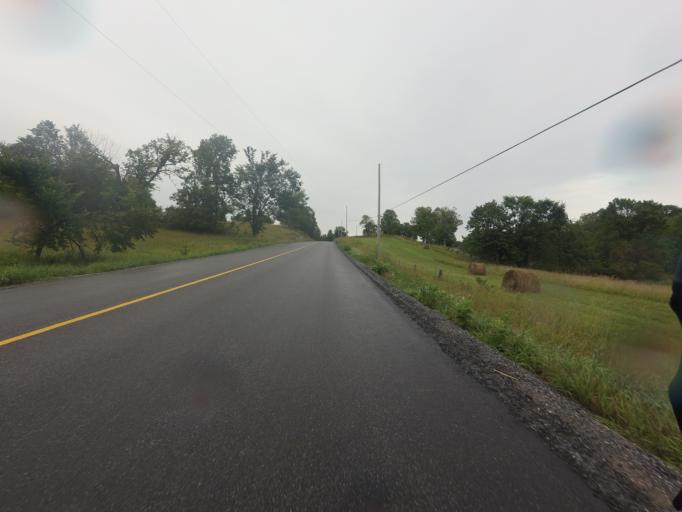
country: CA
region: Ontario
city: Perth
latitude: 44.9210
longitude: -76.4735
